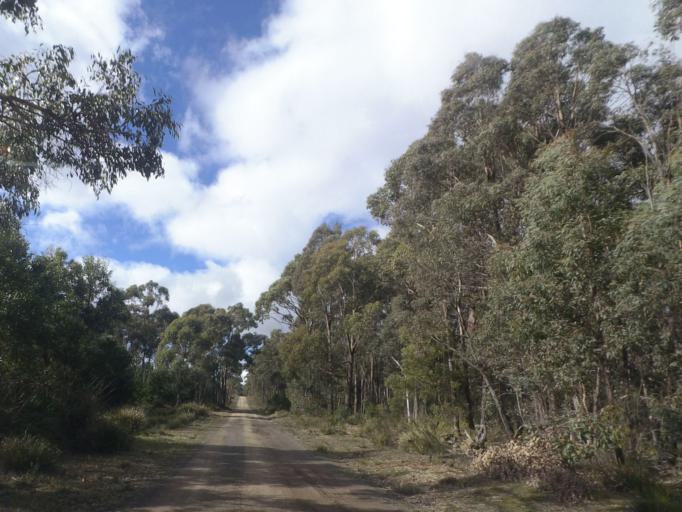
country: AU
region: Victoria
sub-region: Moorabool
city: Bacchus Marsh
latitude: -37.4313
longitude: 144.4458
